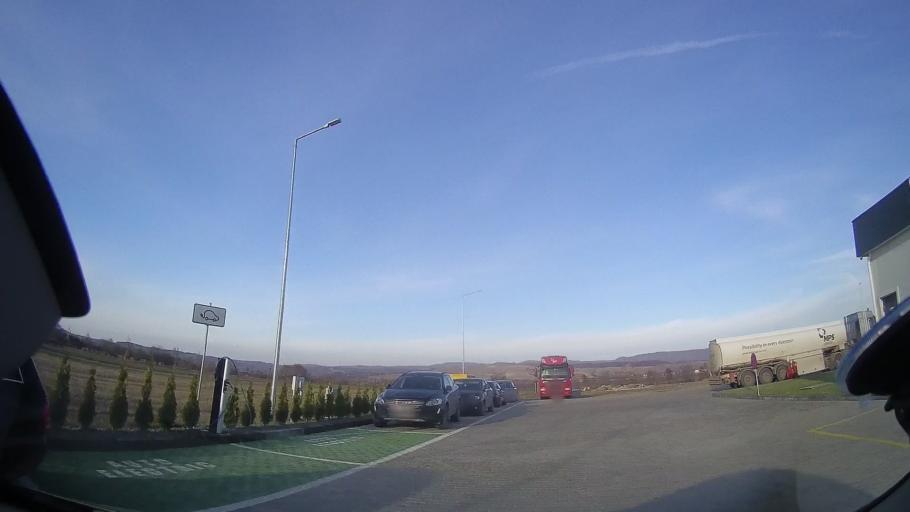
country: RO
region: Bihor
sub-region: Comuna Astileu
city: Astileu
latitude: 47.0413
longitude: 22.3640
